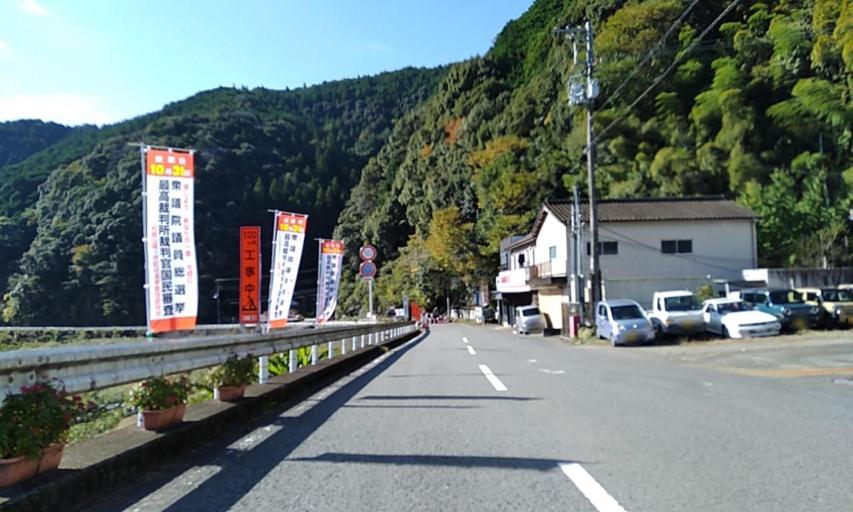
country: JP
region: Wakayama
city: Kainan
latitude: 34.0705
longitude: 135.3556
